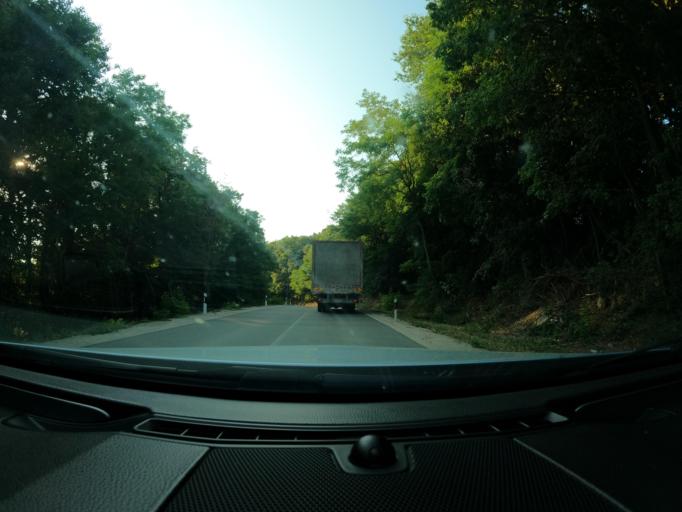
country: RS
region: Autonomna Pokrajina Vojvodina
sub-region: Juznobacki Okrug
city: Beocin
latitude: 45.1424
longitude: 19.7205
